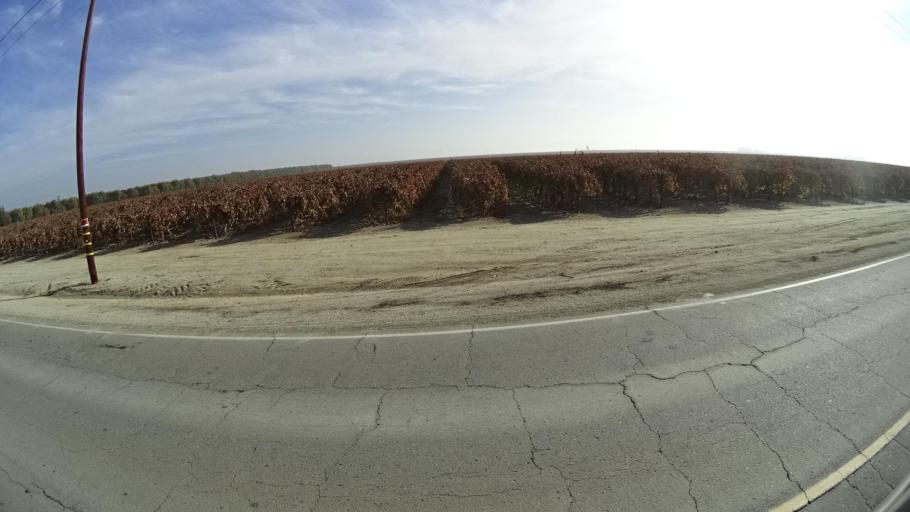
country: US
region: California
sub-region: Kern County
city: McFarland
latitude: 35.6149
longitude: -119.2044
